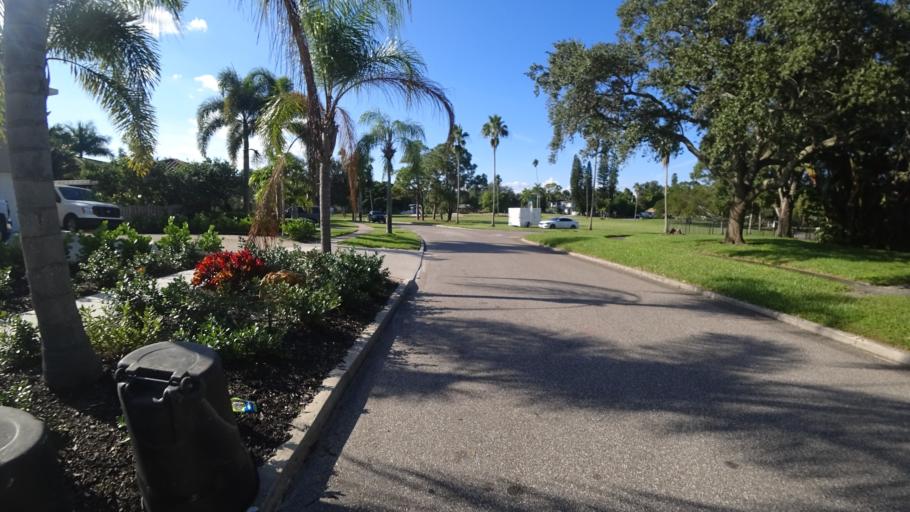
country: US
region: Florida
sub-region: Manatee County
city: West Bradenton
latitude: 27.4918
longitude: -82.6408
